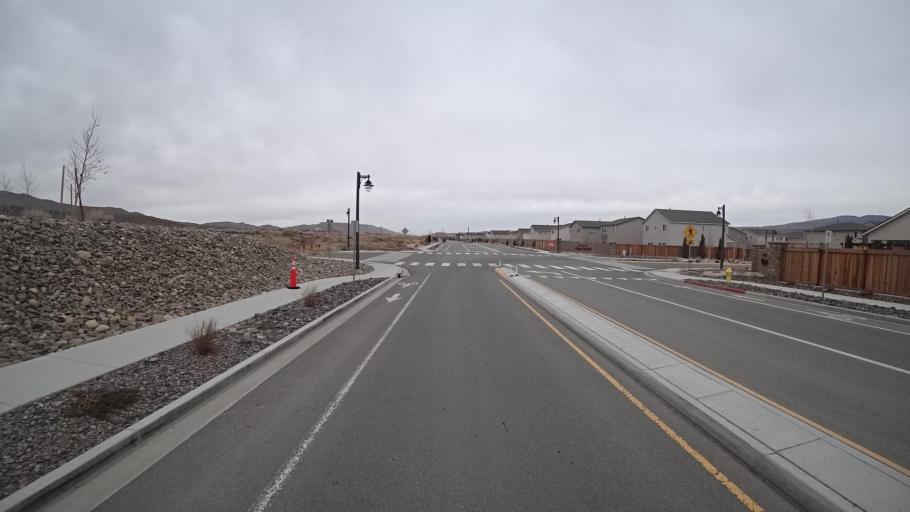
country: US
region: Nevada
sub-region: Washoe County
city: Spanish Springs
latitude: 39.6106
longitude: -119.7199
